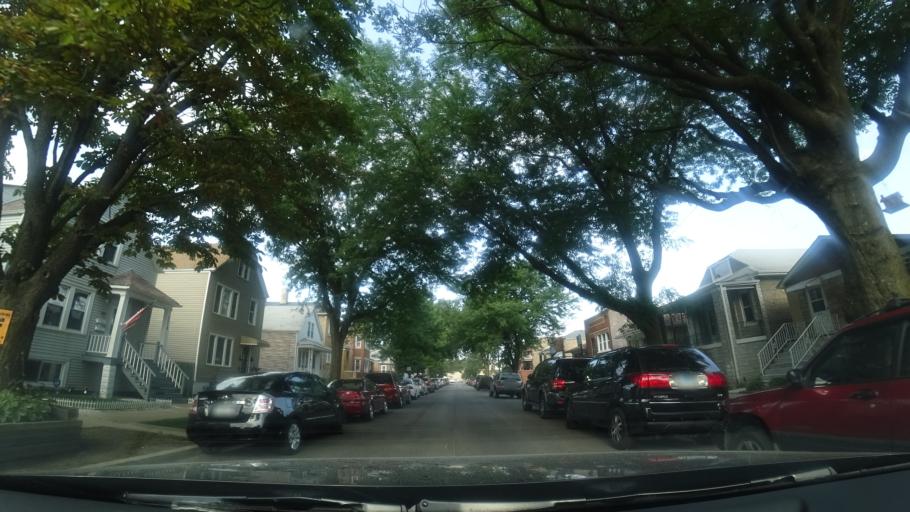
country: US
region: Illinois
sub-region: Cook County
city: Elmwood Park
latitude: 41.9285
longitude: -87.7644
